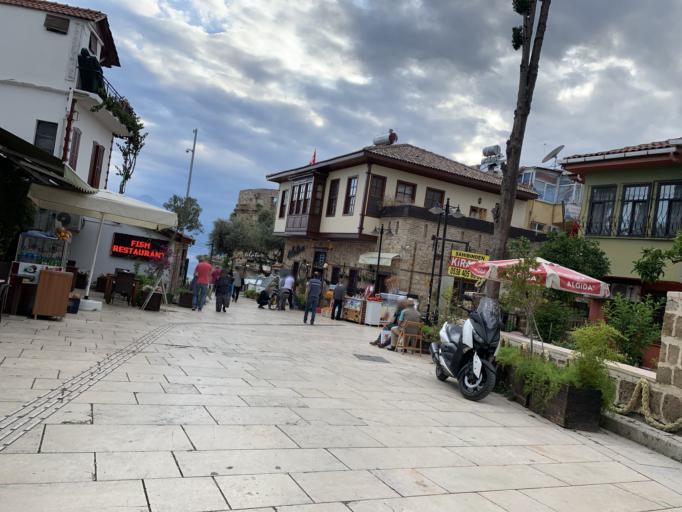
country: TR
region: Antalya
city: Antalya
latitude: 36.8814
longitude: 30.7043
